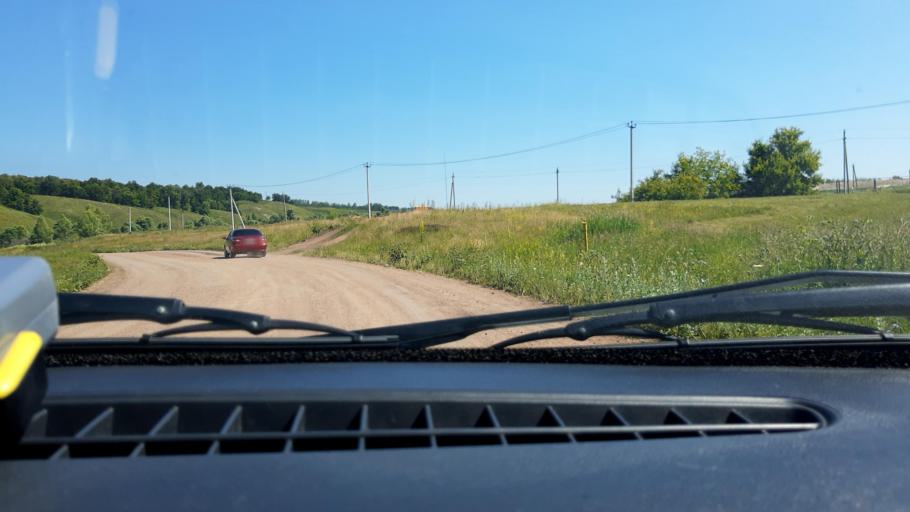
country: RU
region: Bashkortostan
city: Karmaskaly
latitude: 54.3569
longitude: 55.9024
